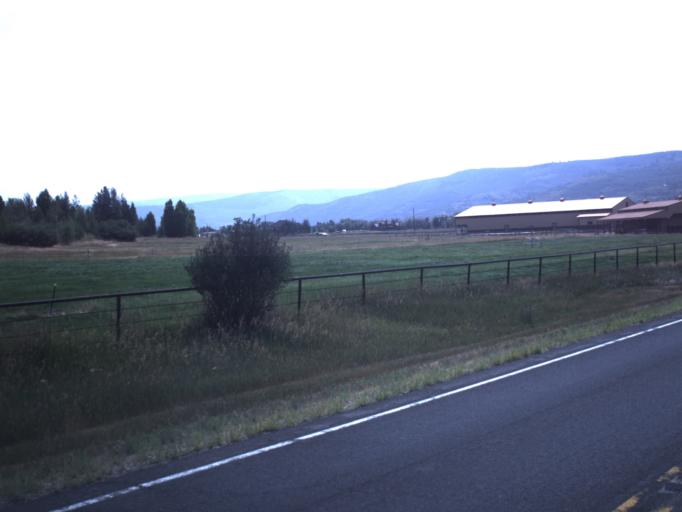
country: US
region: Utah
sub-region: Summit County
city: Francis
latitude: 40.5949
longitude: -111.2423
